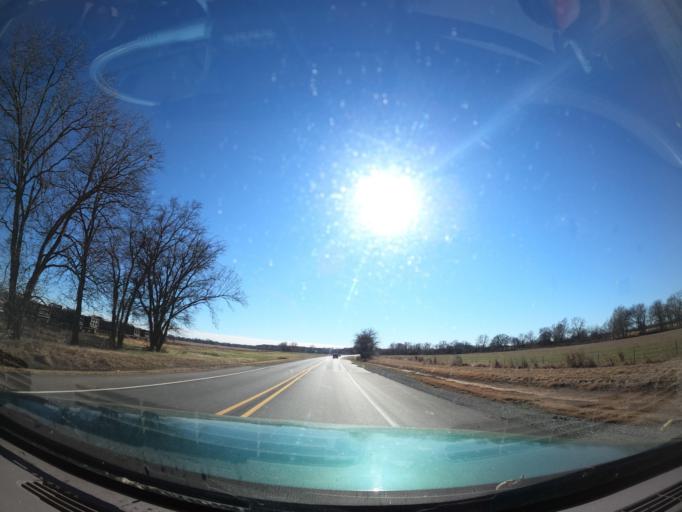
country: US
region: Oklahoma
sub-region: Muskogee County
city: Haskell
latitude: 35.8834
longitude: -95.6598
